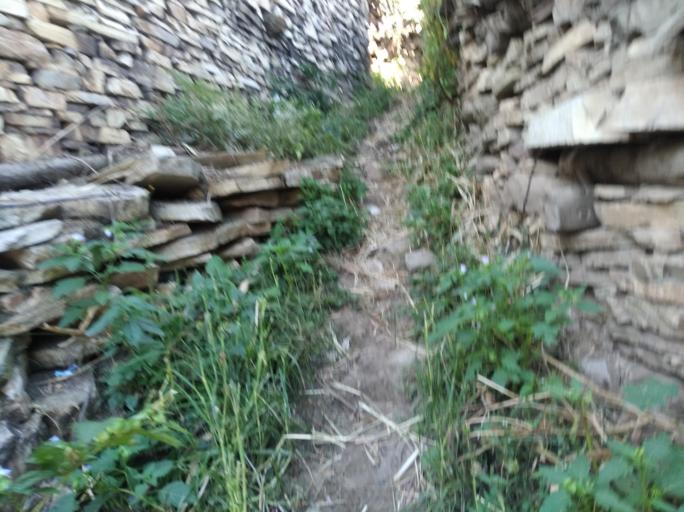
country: NP
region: Western Region
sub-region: Dhawalagiri Zone
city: Jomsom
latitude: 28.8797
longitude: 82.9825
